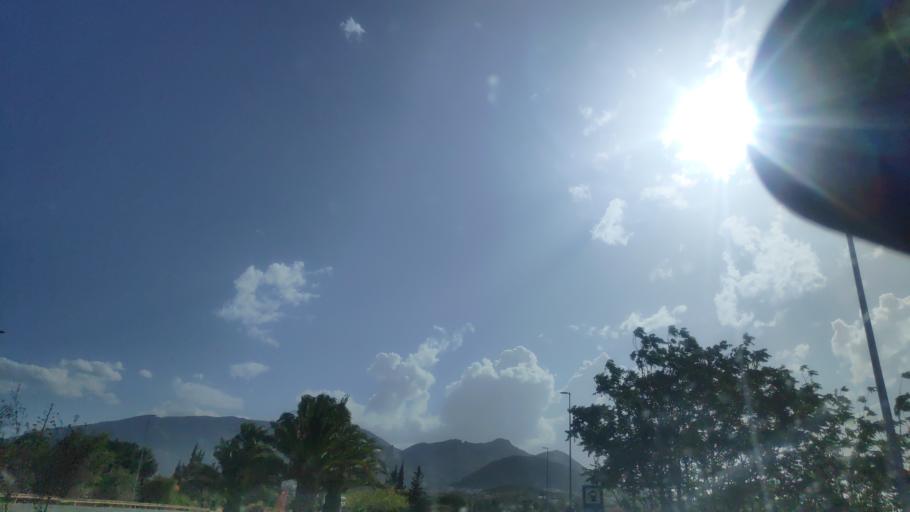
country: ES
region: Andalusia
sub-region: Provincia de Jaen
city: Jaen
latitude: 37.7750
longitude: -3.7615
